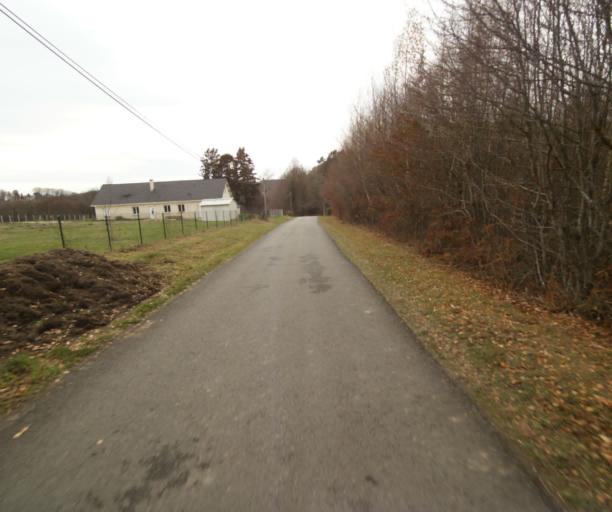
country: FR
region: Limousin
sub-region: Departement de la Correze
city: Chameyrat
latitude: 45.2492
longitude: 1.6729
